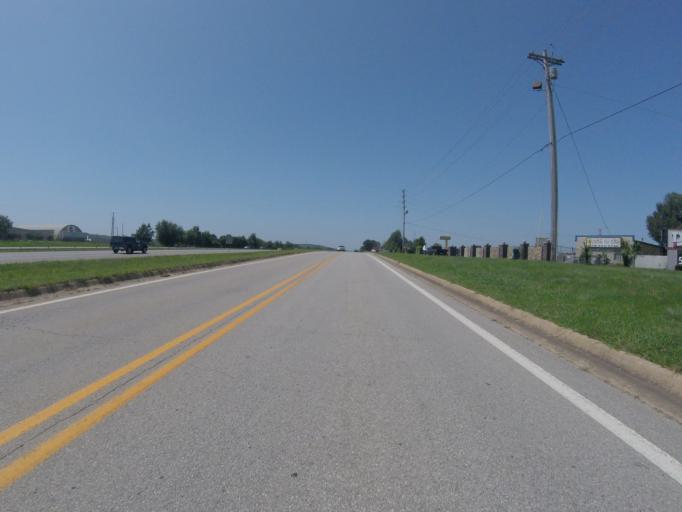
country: US
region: Arkansas
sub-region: Washington County
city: Johnson
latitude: 36.0981
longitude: -94.1869
